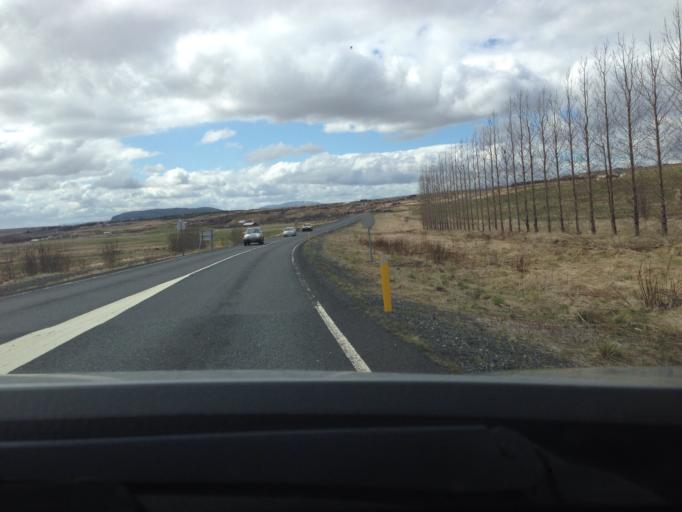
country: IS
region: South
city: Selfoss
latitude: 64.1769
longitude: -20.4558
